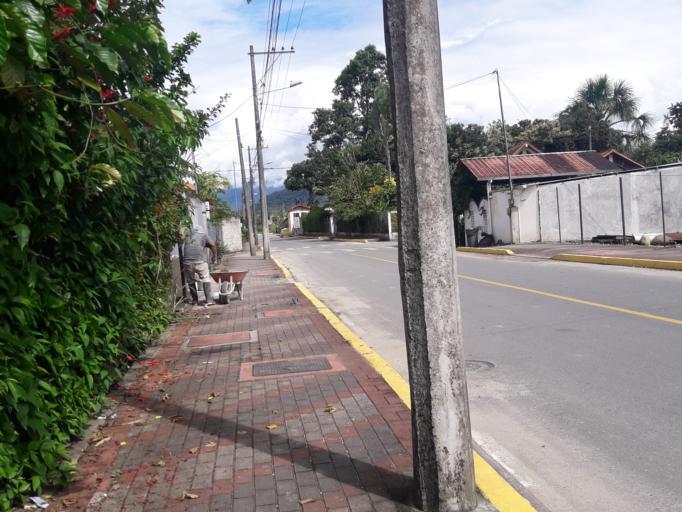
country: EC
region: Napo
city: Tena
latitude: -1.0061
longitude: -77.8159
